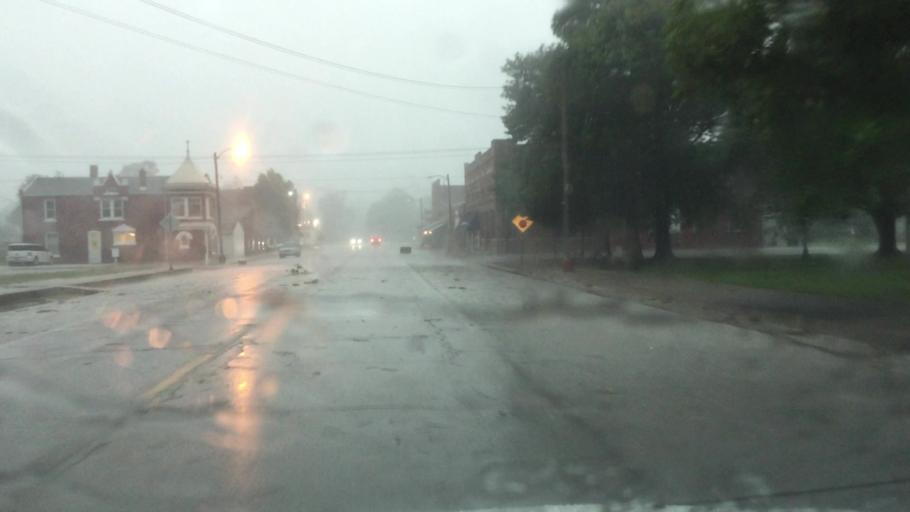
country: US
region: Illinois
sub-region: Adams County
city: Camp Point
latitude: 40.2316
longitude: -91.0626
